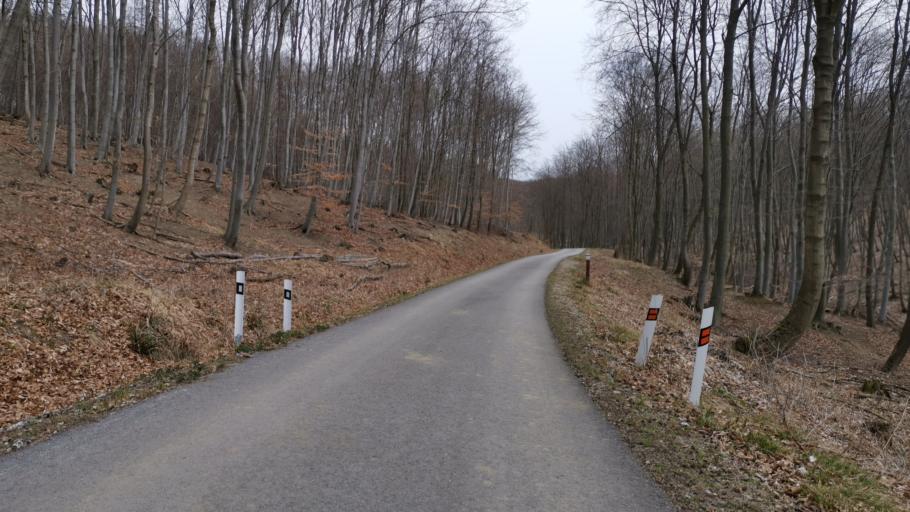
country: CZ
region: South Moravian
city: Straznice
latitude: 48.8156
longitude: 17.3391
